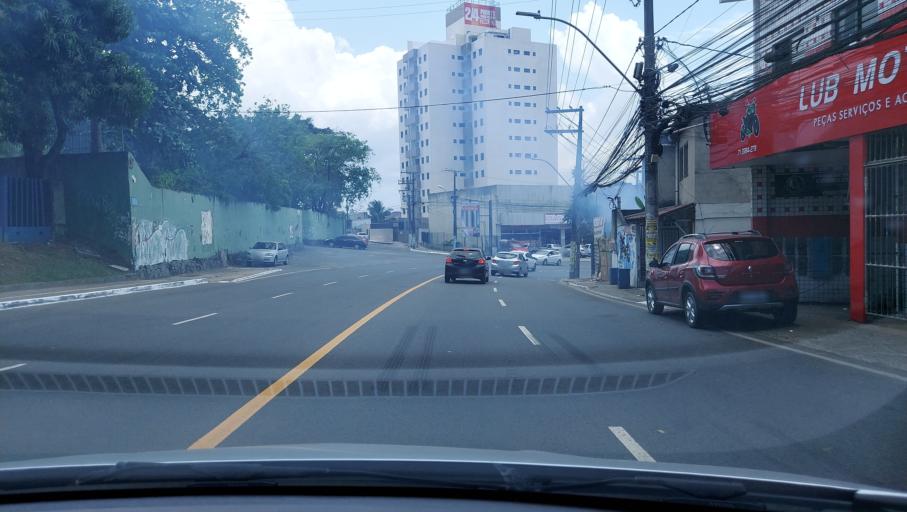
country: BR
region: Bahia
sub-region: Salvador
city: Salvador
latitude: -12.9583
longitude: -38.4673
